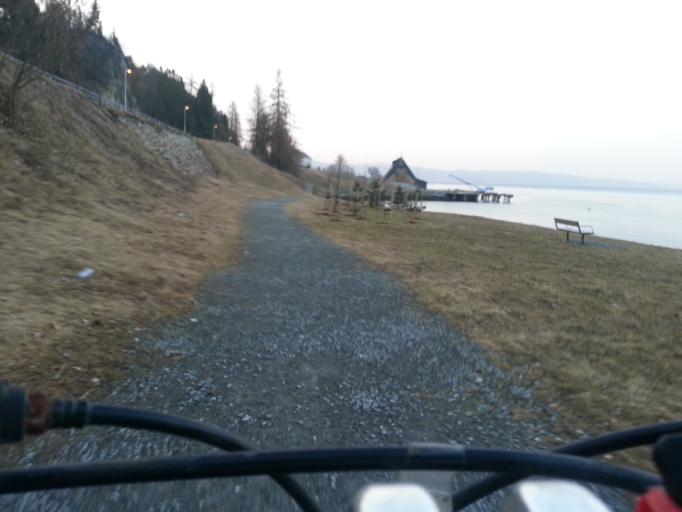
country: NO
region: Sor-Trondelag
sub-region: Trondheim
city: Trondheim
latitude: 63.4341
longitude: 10.3507
